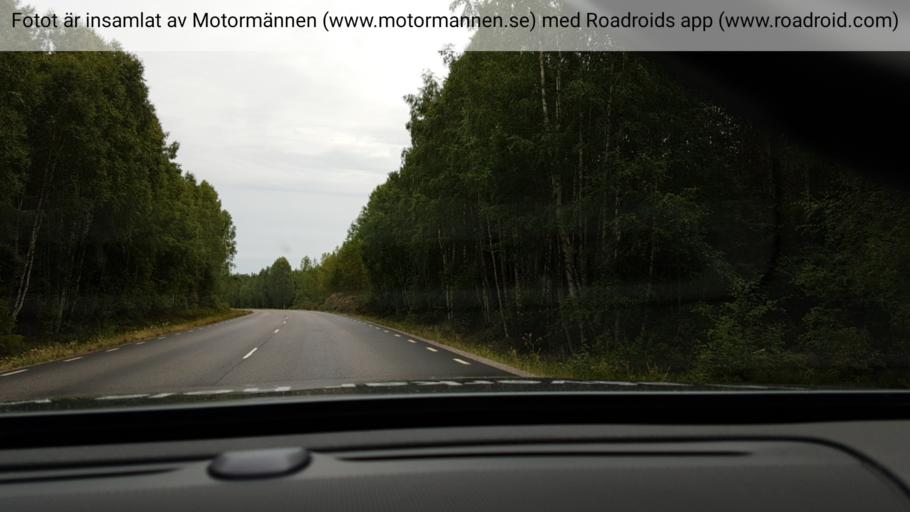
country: SE
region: Dalarna
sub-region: Ludvika Kommun
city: Ludvika
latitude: 60.2914
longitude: 15.2344
